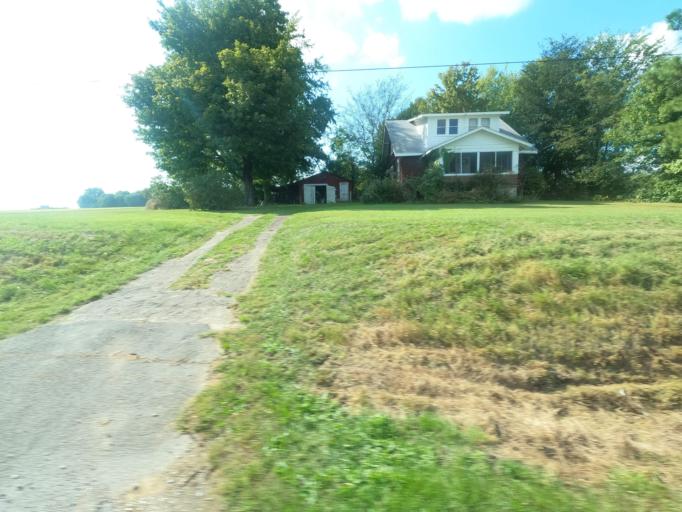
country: US
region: Illinois
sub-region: Massac County
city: Metropolis
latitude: 37.1880
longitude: -88.6766
